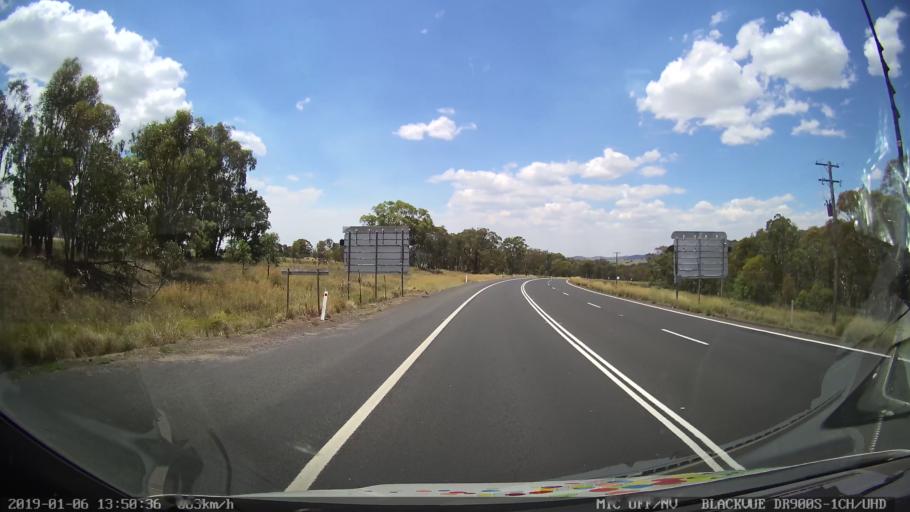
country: AU
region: New South Wales
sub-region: Tamworth Municipality
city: Kootingal
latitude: -30.9330
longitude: 151.1132
